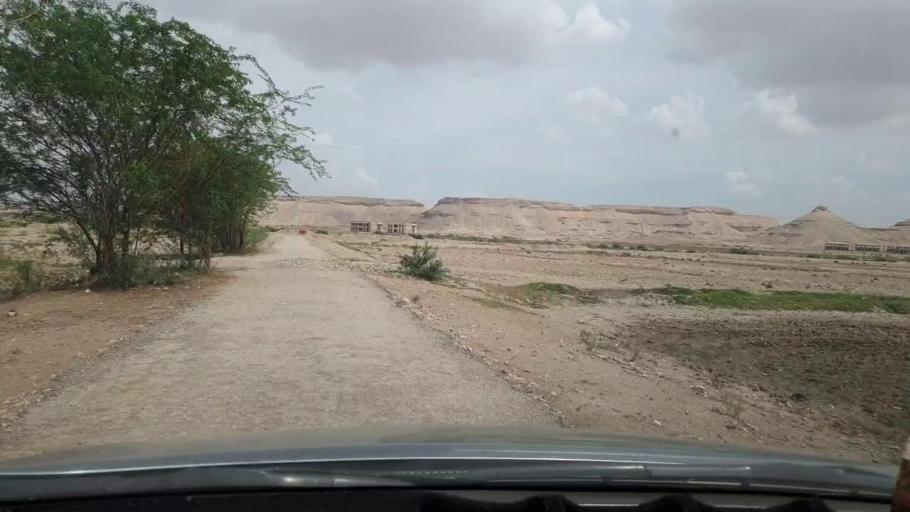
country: PK
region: Sindh
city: Khairpur
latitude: 27.4757
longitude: 68.8593
